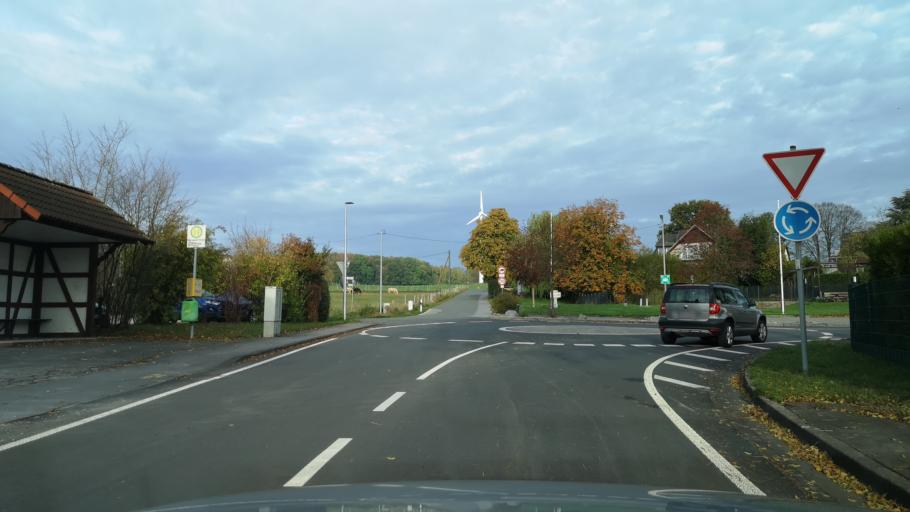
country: DE
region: North Rhine-Westphalia
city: Wickede
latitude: 51.4437
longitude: 7.8474
